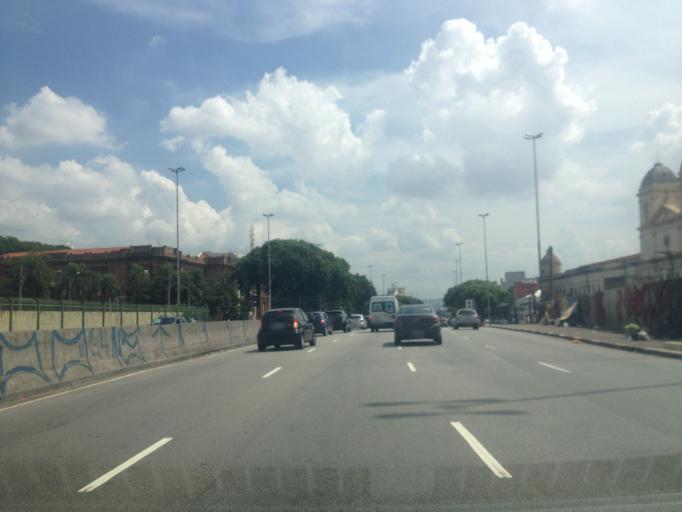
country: BR
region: Sao Paulo
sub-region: Sao Paulo
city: Sao Paulo
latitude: -23.5360
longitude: -46.6336
